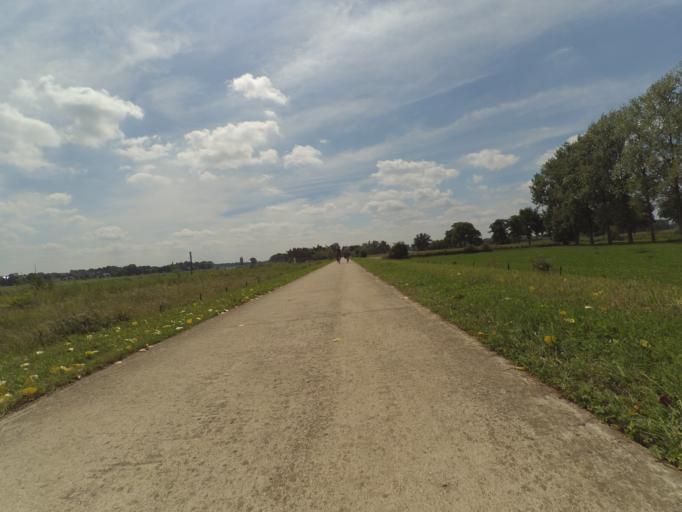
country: NL
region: Limburg
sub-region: Gemeente Stein
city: Berg
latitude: 51.0146
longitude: 5.7663
